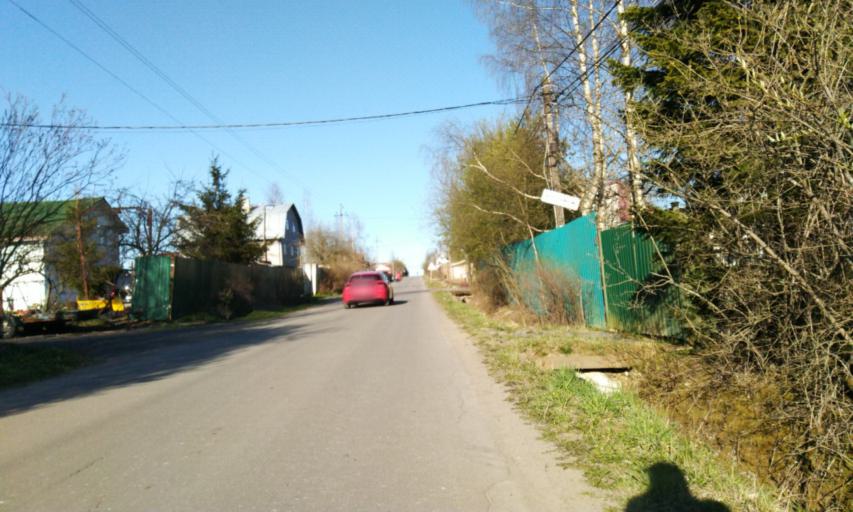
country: RU
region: Leningrad
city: Toksovo
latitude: 60.1449
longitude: 30.5606
